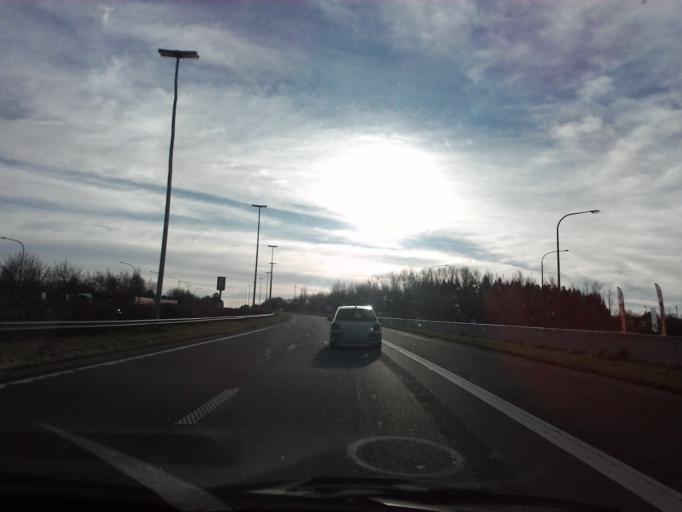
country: BE
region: Wallonia
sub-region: Province de Liege
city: Sprimont
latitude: 50.5242
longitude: 5.6649
